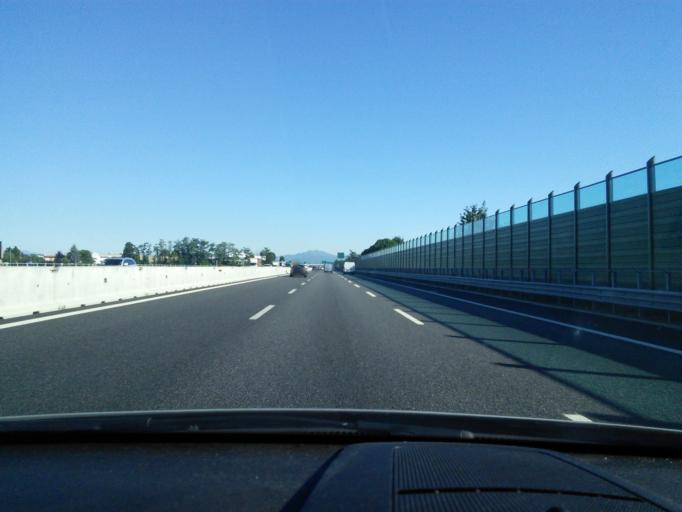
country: IT
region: Lombardy
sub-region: Provincia di Varese
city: Origgio
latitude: 45.5933
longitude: 9.0120
